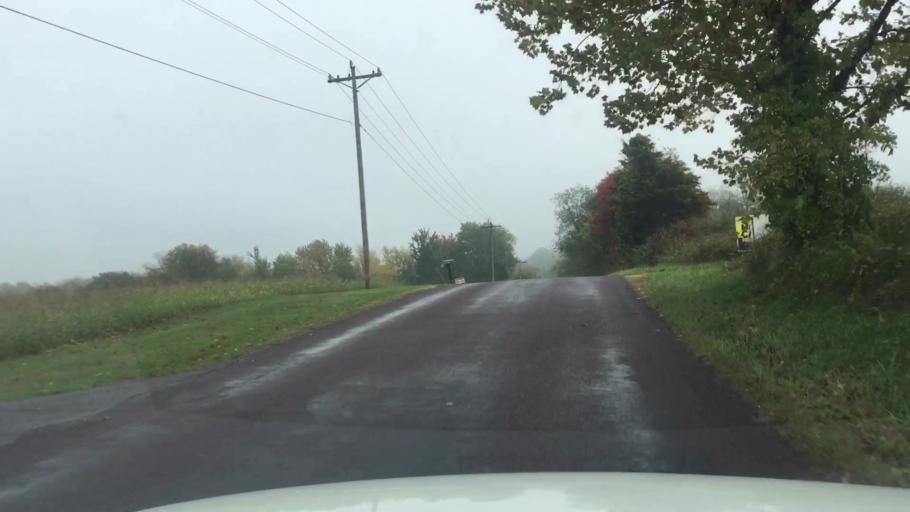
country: US
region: Missouri
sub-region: Boone County
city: Columbia
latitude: 38.8559
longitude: -92.3587
